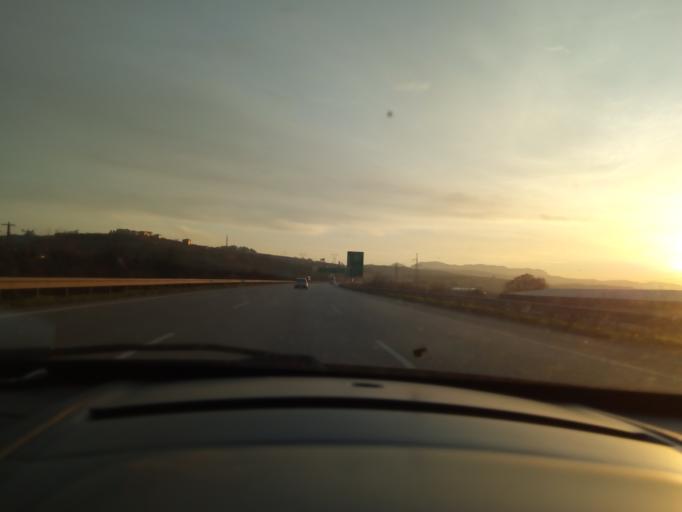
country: TR
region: Bursa
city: Niluefer
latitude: 40.2882
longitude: 29.0077
